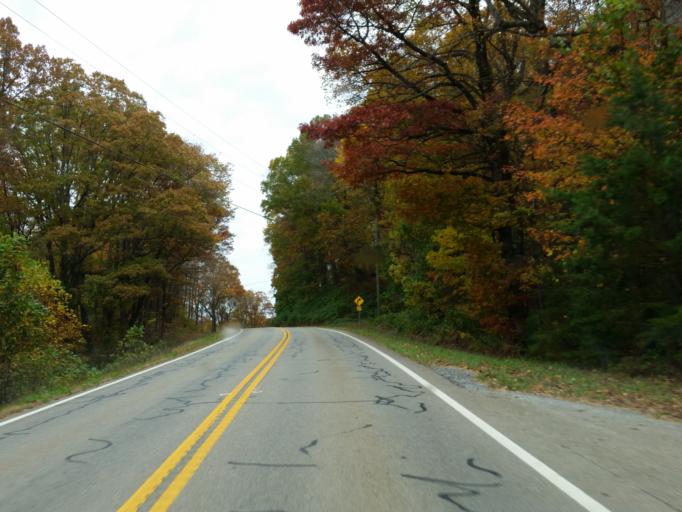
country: US
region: Georgia
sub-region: Pickens County
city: Jasper
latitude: 34.5349
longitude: -84.3758
